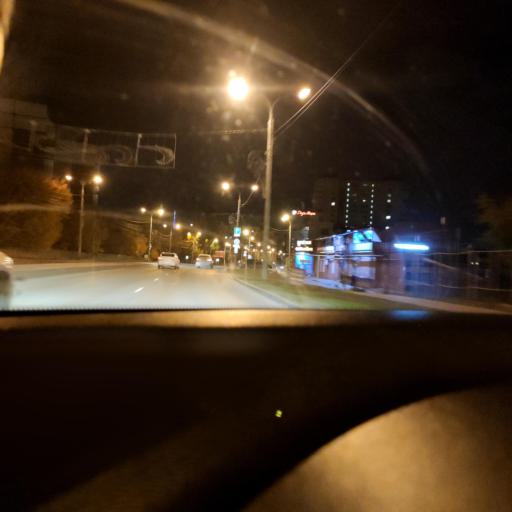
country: RU
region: Samara
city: Samara
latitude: 53.2518
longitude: 50.2014
